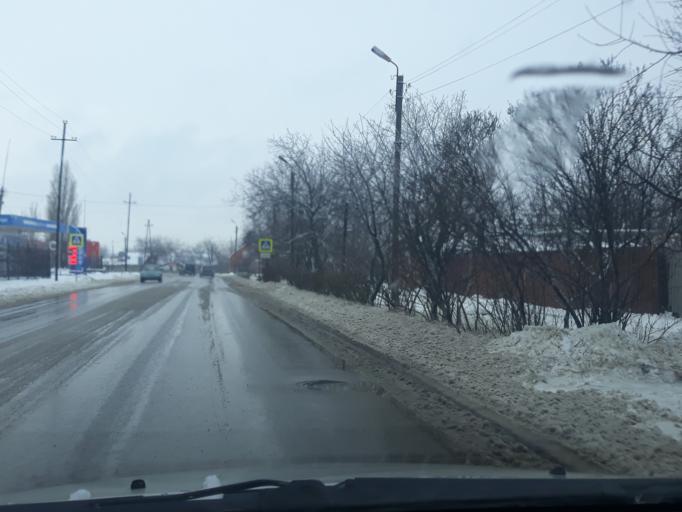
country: RU
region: Rostov
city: Taganrog
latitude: 47.2279
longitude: 38.8900
